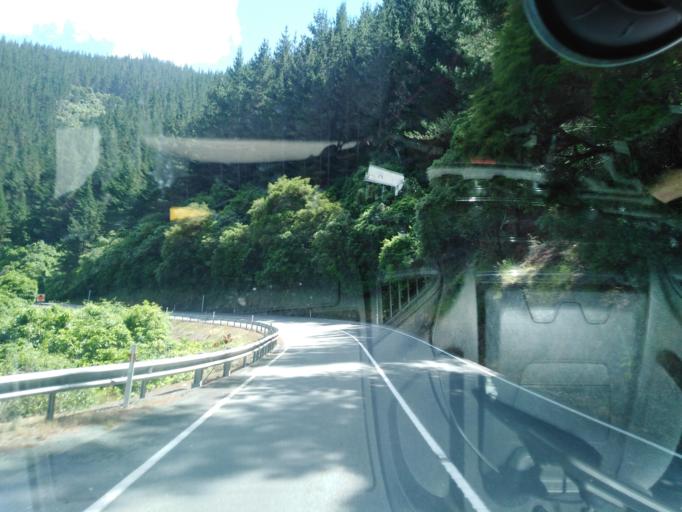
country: NZ
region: Nelson
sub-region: Nelson City
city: Nelson
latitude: -41.2277
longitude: 173.4208
